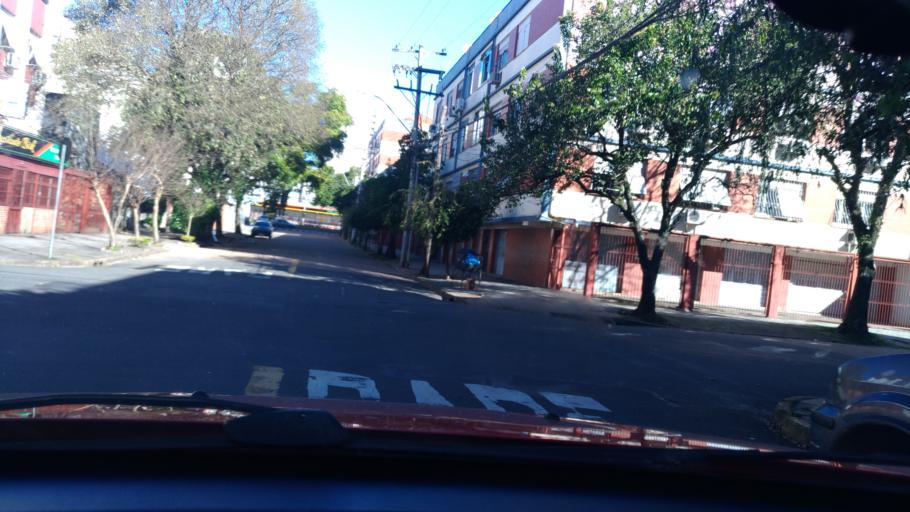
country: BR
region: Rio Grande do Sul
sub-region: Porto Alegre
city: Porto Alegre
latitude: -30.0101
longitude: -51.1638
